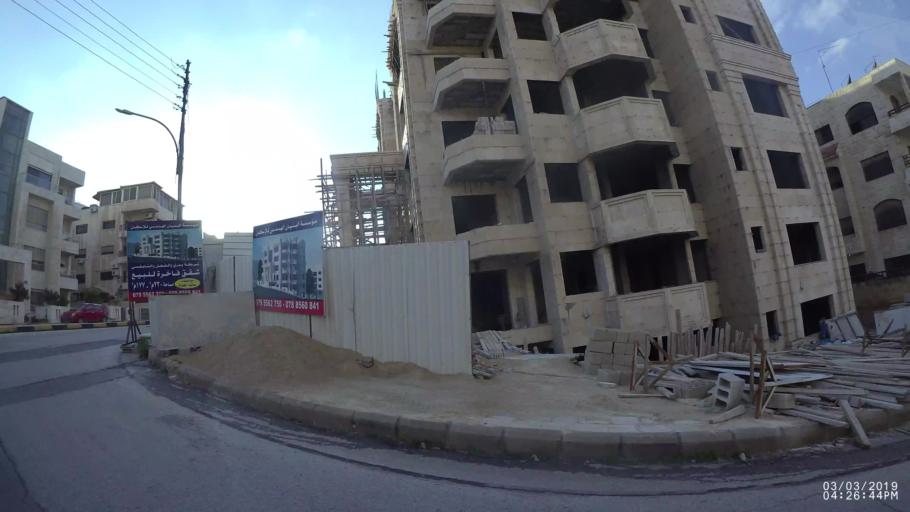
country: JO
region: Amman
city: Al Jubayhah
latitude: 31.9768
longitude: 35.8811
